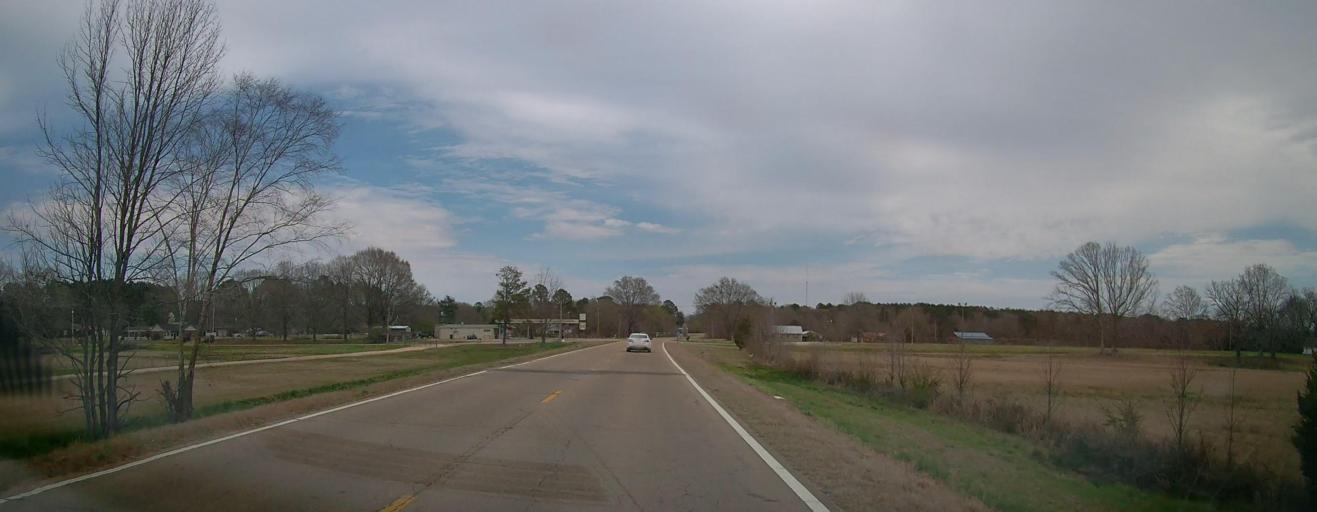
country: US
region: Mississippi
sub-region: Itawamba County
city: Mantachie
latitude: 34.2669
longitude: -88.5602
